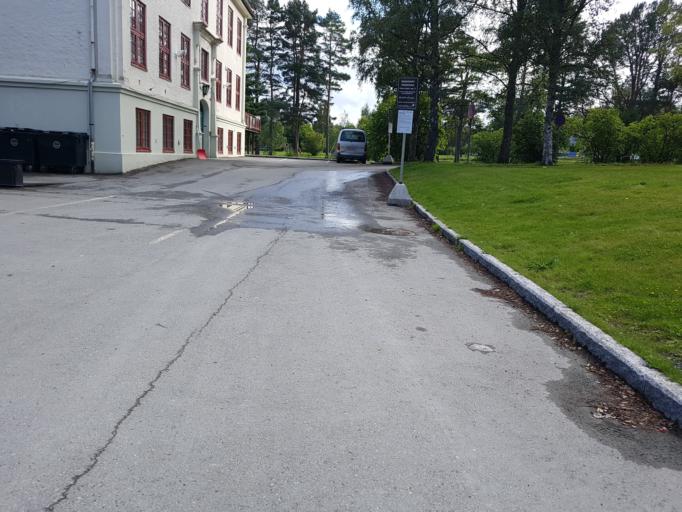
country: NO
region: Sor-Trondelag
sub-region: Trondheim
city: Trondheim
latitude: 63.4290
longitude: 10.4376
